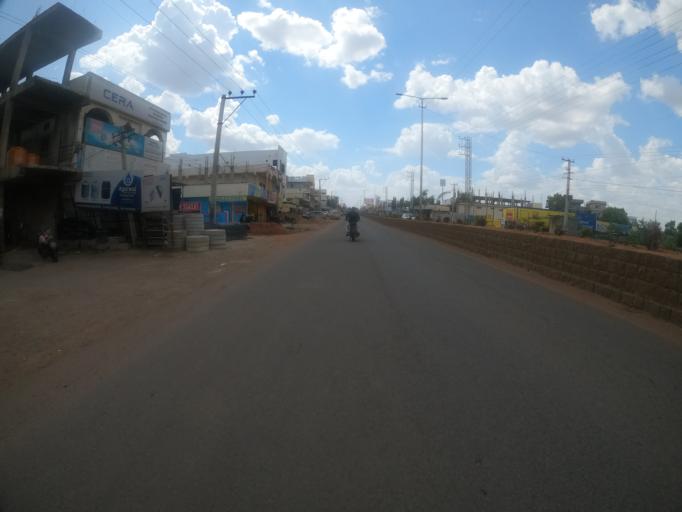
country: IN
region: Telangana
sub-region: Rangareddi
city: Sriramnagar
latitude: 17.3083
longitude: 78.1432
